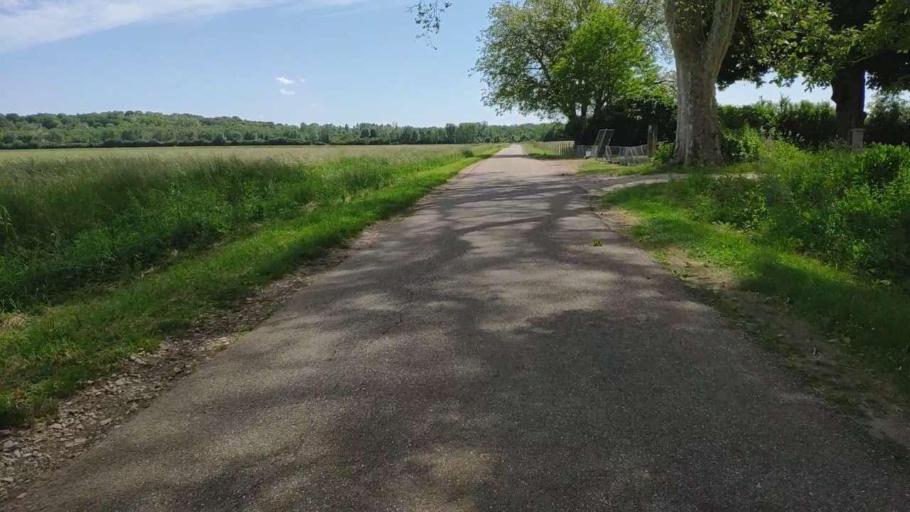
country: FR
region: Franche-Comte
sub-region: Departement du Jura
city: Bletterans
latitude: 46.7285
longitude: 5.4798
